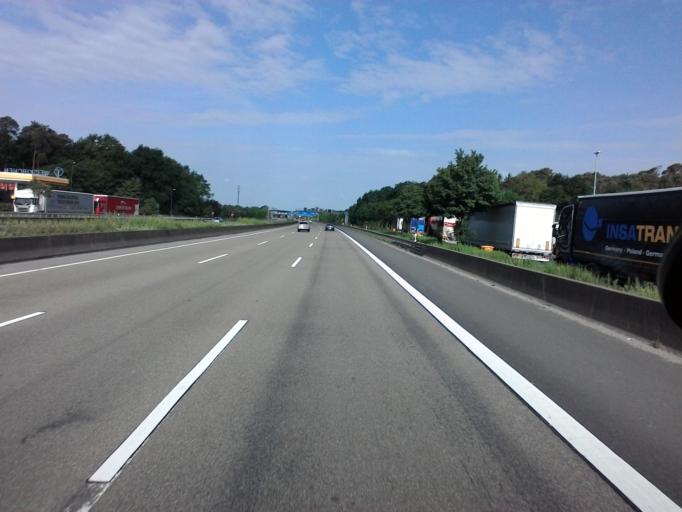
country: DE
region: Hesse
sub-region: Regierungsbezirk Darmstadt
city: Rodgau
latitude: 50.0557
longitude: 8.9082
